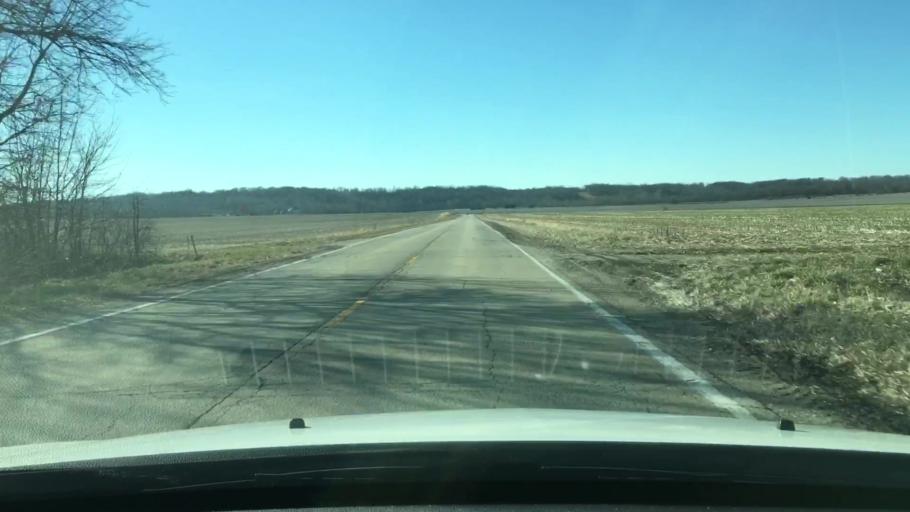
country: US
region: Illinois
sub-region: Mason County
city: Havana
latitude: 40.2829
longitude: -90.1652
